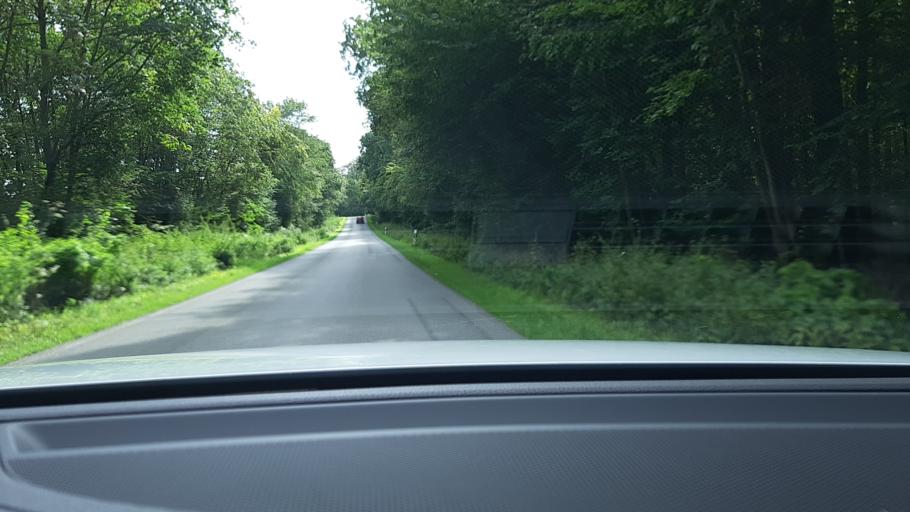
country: DE
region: Schleswig-Holstein
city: Reinfeld
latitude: 53.8473
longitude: 10.4711
